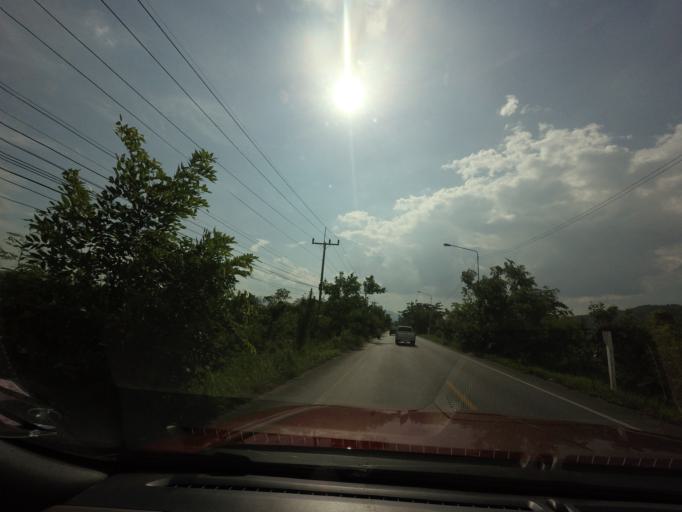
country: TH
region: Yala
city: Yala
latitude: 6.5528
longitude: 101.2282
